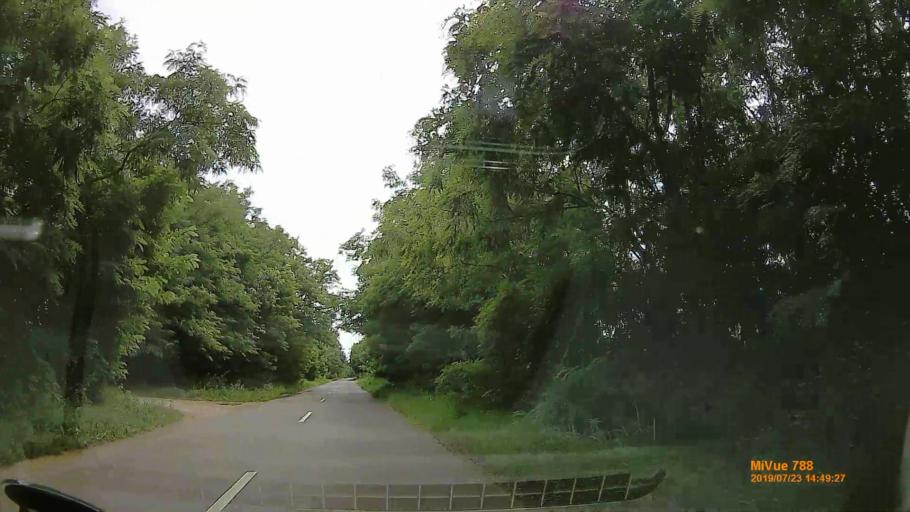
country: HU
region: Szabolcs-Szatmar-Bereg
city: Kalmanhaza
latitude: 47.8957
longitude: 21.6624
